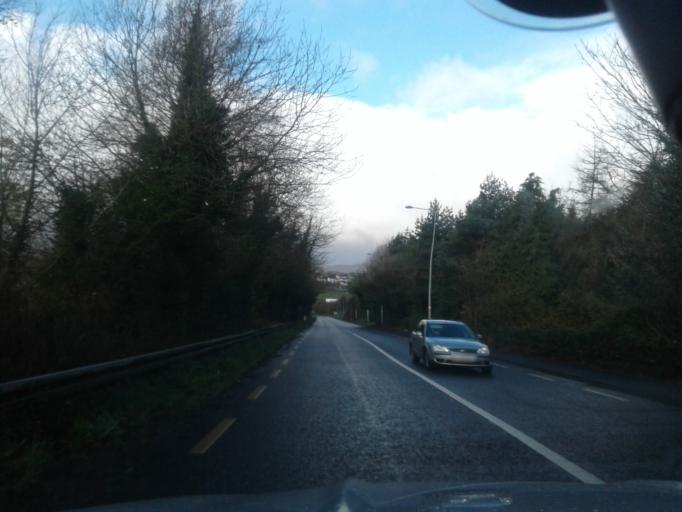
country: IE
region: Ulster
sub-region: County Donegal
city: Letterkenny
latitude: 54.9581
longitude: -7.6971
